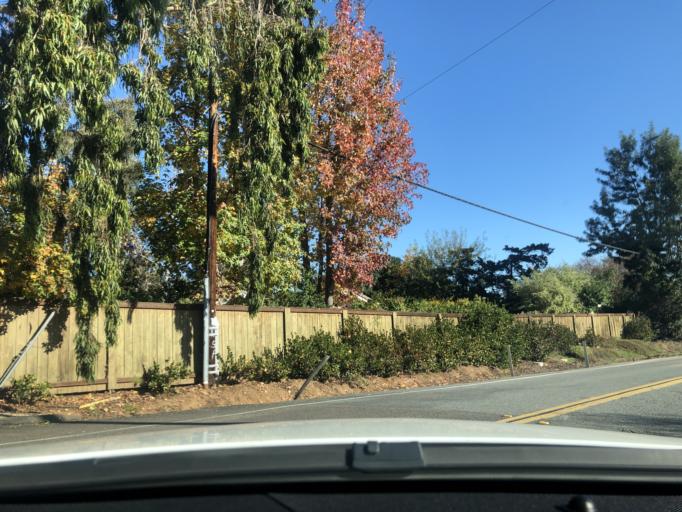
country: US
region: California
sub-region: San Diego County
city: Rancho San Diego
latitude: 32.7694
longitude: -116.9385
